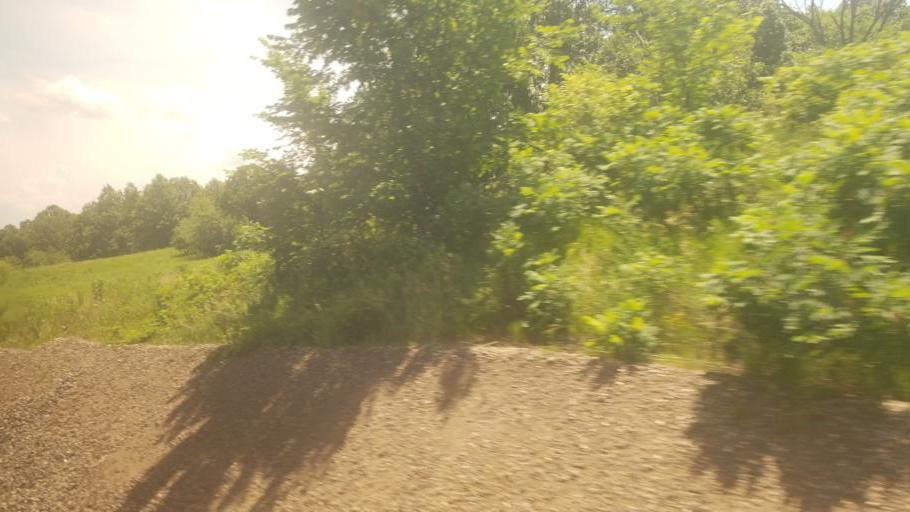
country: US
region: Missouri
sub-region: Linn County
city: Marceline
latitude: 39.8685
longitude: -92.7814
